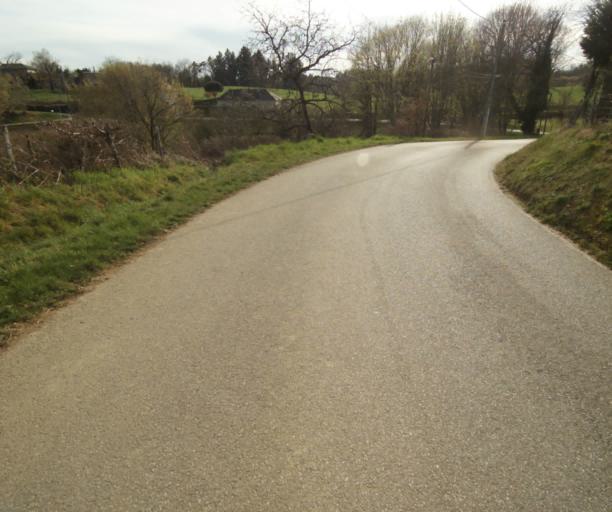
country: FR
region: Limousin
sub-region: Departement de la Correze
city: Naves
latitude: 45.3052
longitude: 1.7514
